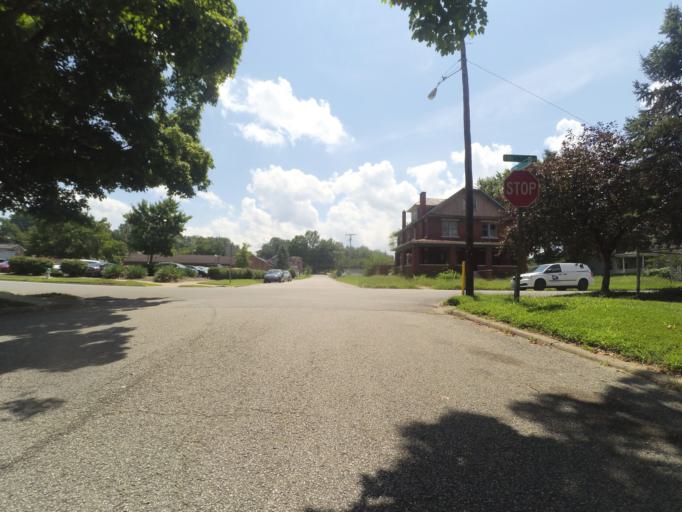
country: US
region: West Virginia
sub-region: Cabell County
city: Huntington
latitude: 38.4147
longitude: -82.4219
